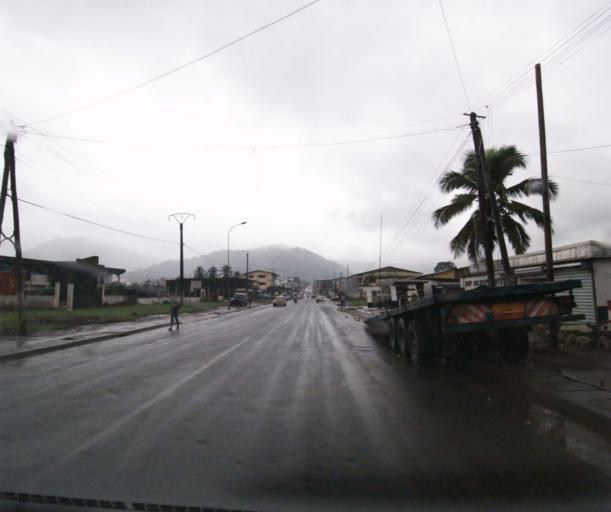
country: CM
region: South-West Province
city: Limbe
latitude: 4.0077
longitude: 9.2126
